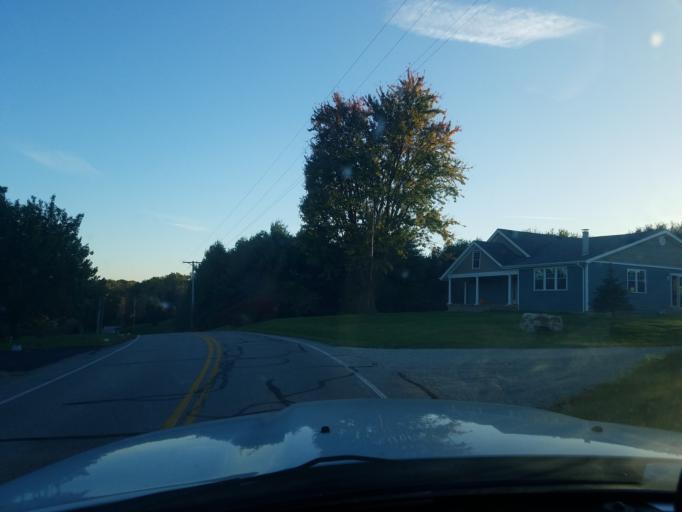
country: US
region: Indiana
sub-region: Floyd County
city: Galena
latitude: 38.3968
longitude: -85.9108
